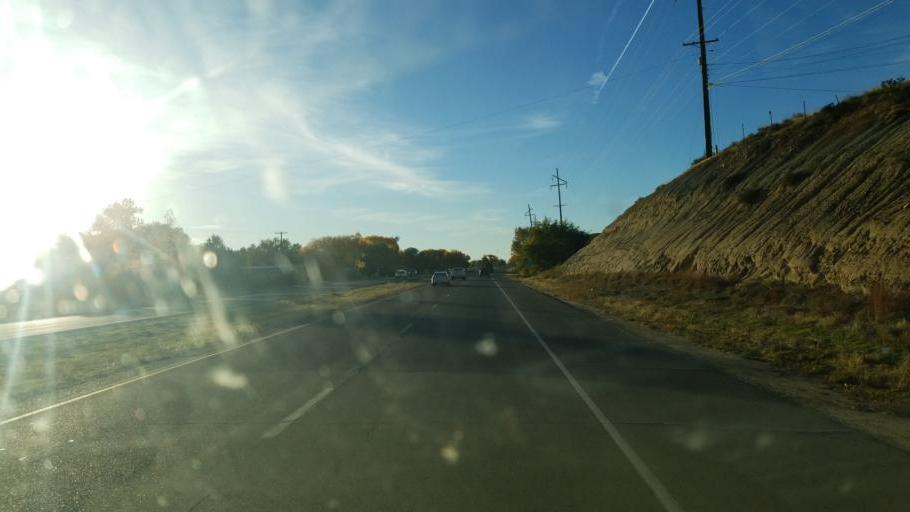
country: US
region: New Mexico
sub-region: San Juan County
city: Lee Acres
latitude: 36.7072
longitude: -108.1237
